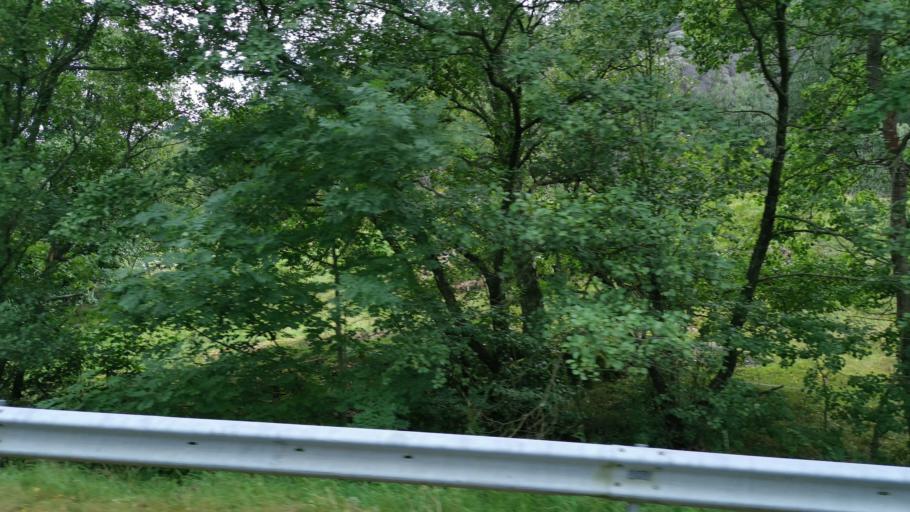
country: SE
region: Vaestra Goetaland
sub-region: Lysekils Kommun
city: Brastad
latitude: 58.4747
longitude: 11.4197
